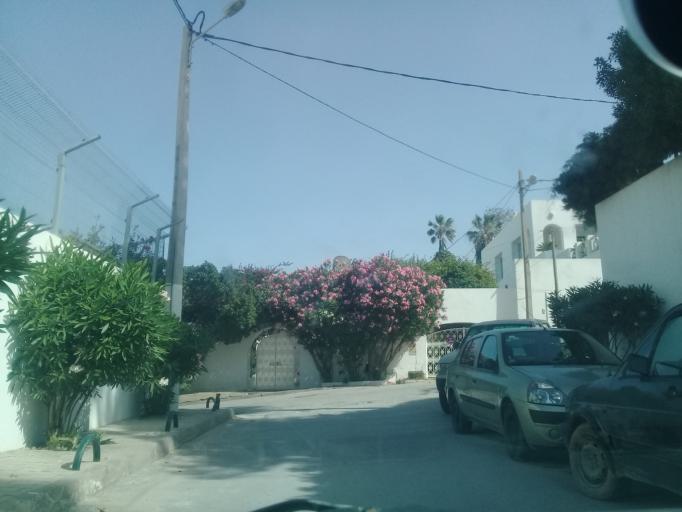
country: TN
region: Tunis
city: Al Marsa
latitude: 36.8900
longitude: 10.3253
